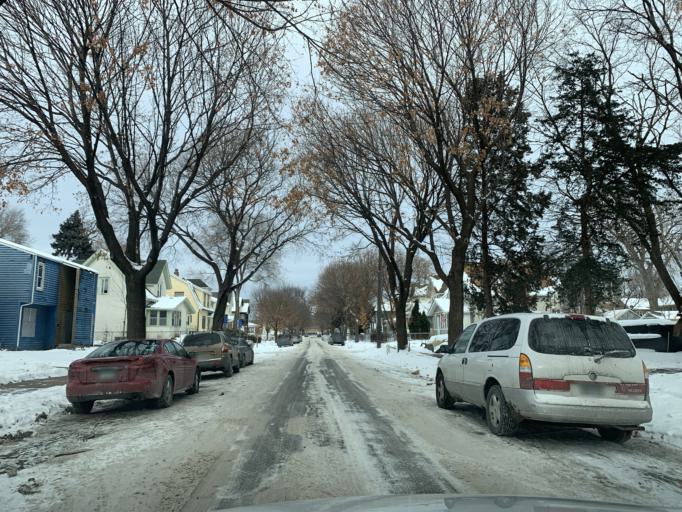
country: US
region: Minnesota
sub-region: Hennepin County
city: Minneapolis
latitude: 44.9896
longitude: -93.3007
